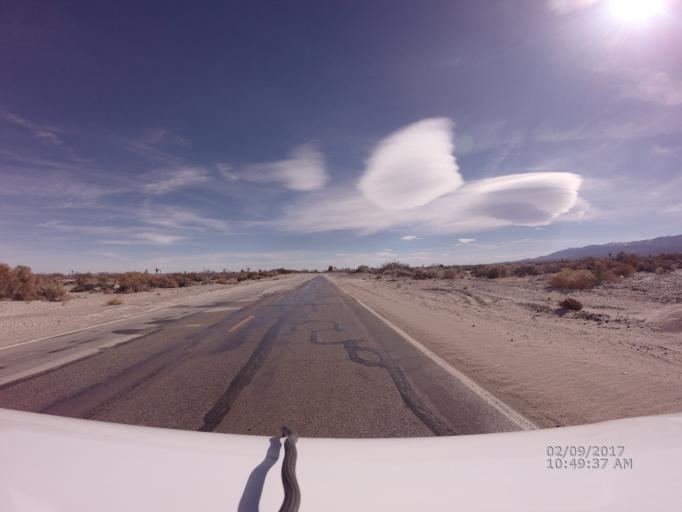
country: US
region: California
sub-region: Los Angeles County
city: Lake Los Angeles
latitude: 34.5424
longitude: -117.8435
